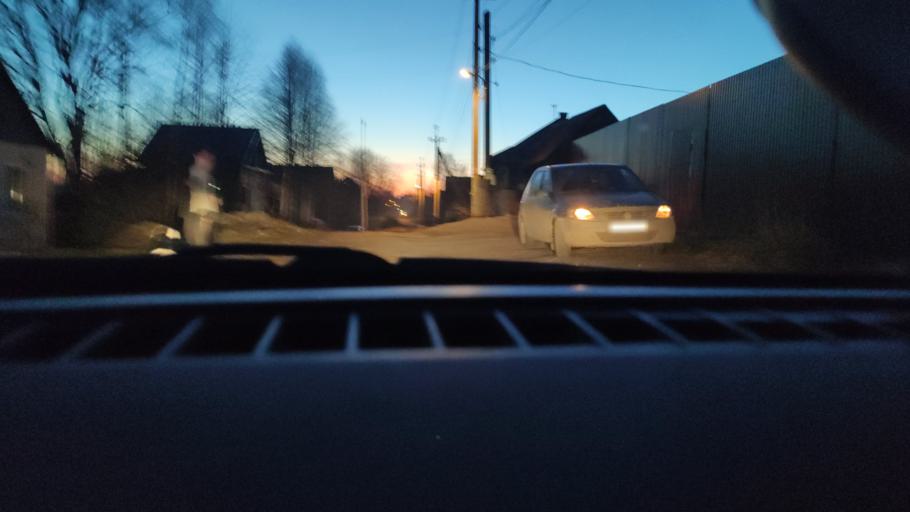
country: RU
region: Perm
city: Perm
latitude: 58.0383
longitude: 56.3400
